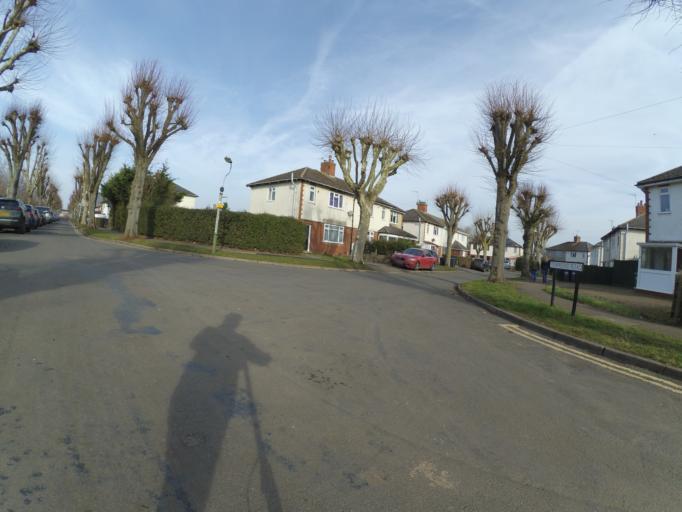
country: GB
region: England
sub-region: Warwickshire
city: Rugby
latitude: 52.3731
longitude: -1.2379
